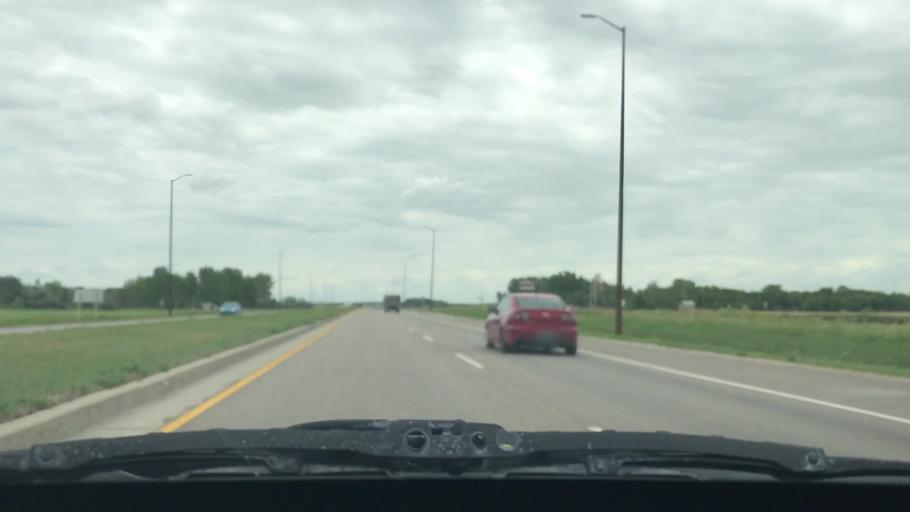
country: CA
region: Manitoba
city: Winnipeg
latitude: 49.8401
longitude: -96.9842
